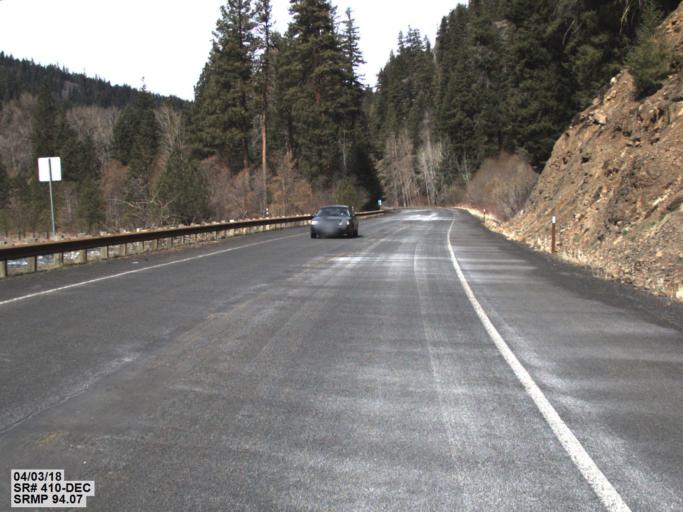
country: US
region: Washington
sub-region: Kittitas County
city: Cle Elum
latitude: 46.9658
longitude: -121.0880
